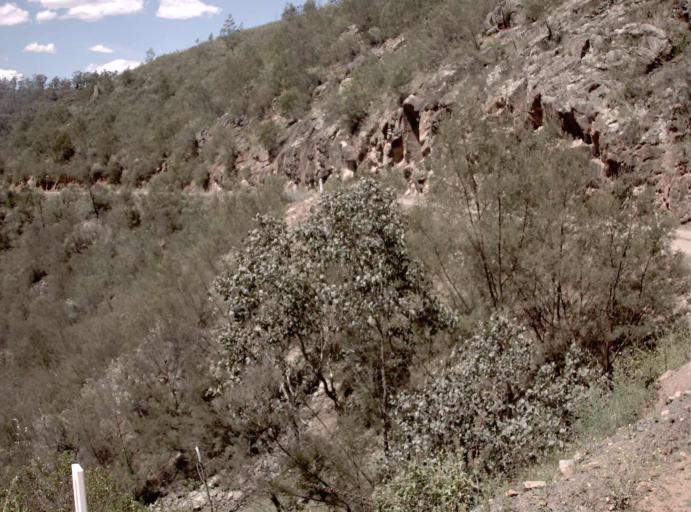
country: AU
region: New South Wales
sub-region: Snowy River
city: Jindabyne
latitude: -37.0368
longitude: 148.5402
